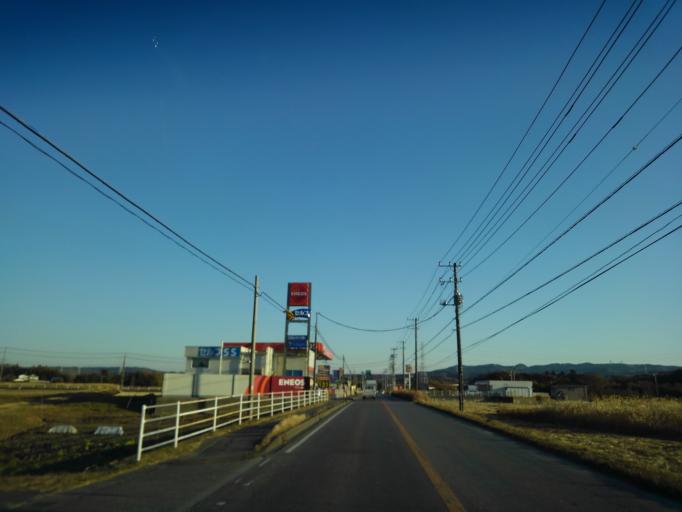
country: JP
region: Chiba
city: Kimitsu
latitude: 35.3151
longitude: 139.9329
